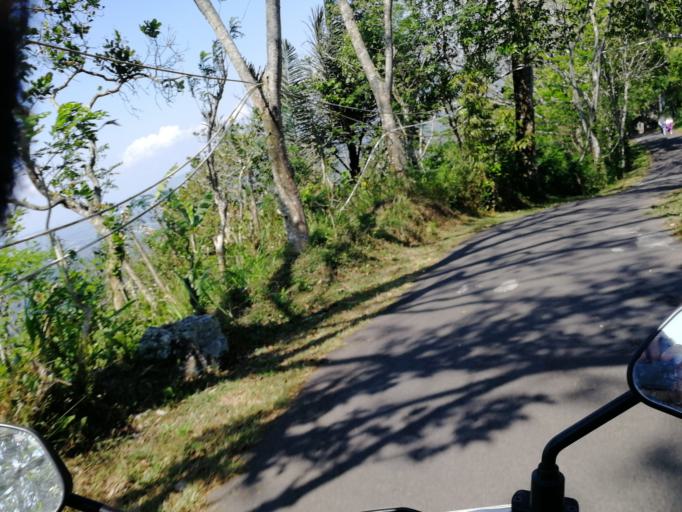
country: ID
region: Bali
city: Tiyingtali Kelod
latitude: -8.3923
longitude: 115.6344
